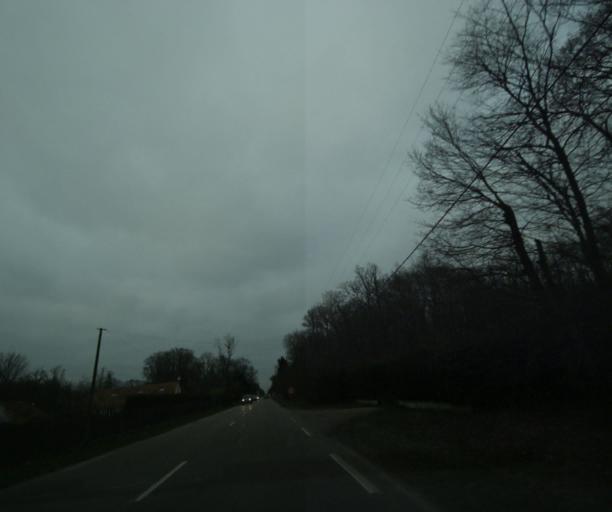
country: FR
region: Ile-de-France
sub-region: Departement des Yvelines
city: Chanteloup-les-Vignes
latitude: 48.9916
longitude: 2.0226
